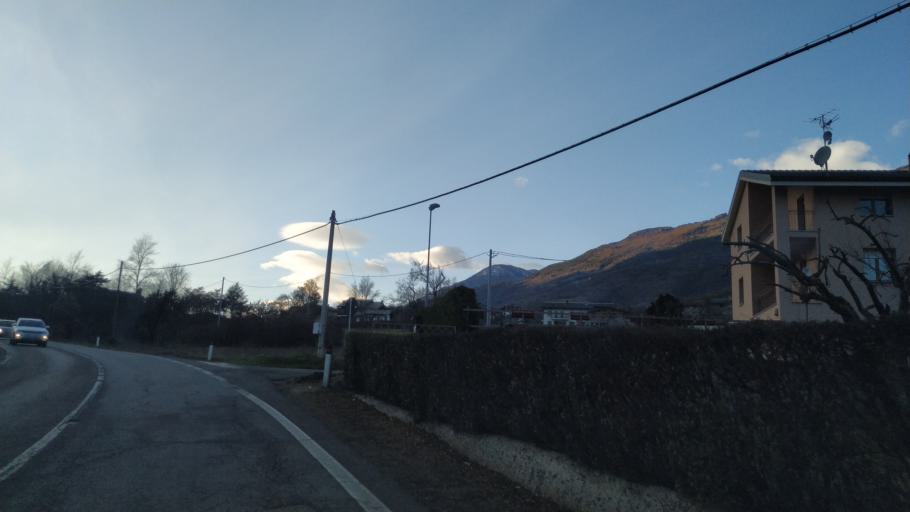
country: IT
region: Aosta Valley
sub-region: Valle d'Aosta
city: Chambave
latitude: 45.7435
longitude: 7.5292
